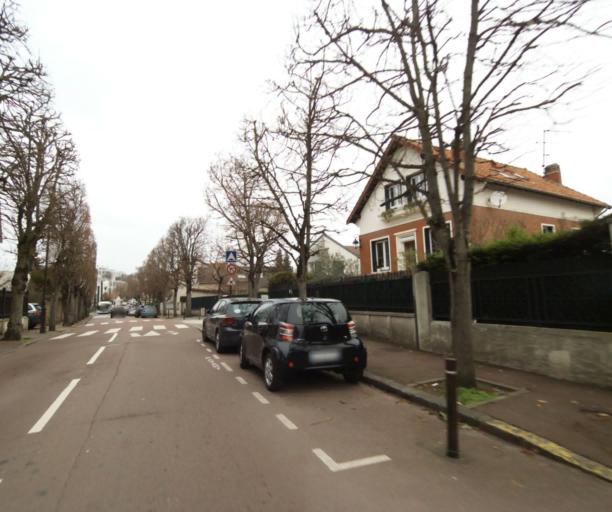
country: FR
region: Ile-de-France
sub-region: Departement des Hauts-de-Seine
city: Saint-Cloud
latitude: 48.8486
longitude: 2.2024
